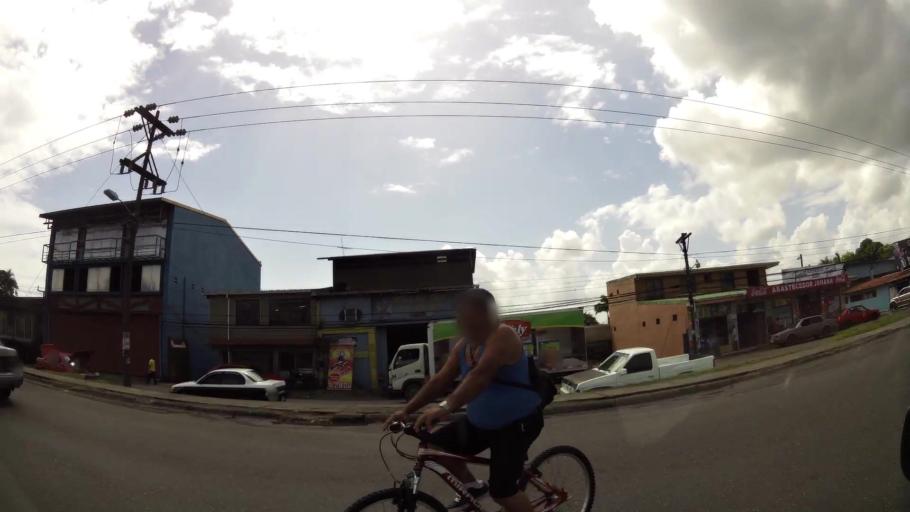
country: CR
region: Limon
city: Limon
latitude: 9.9855
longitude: -83.0469
